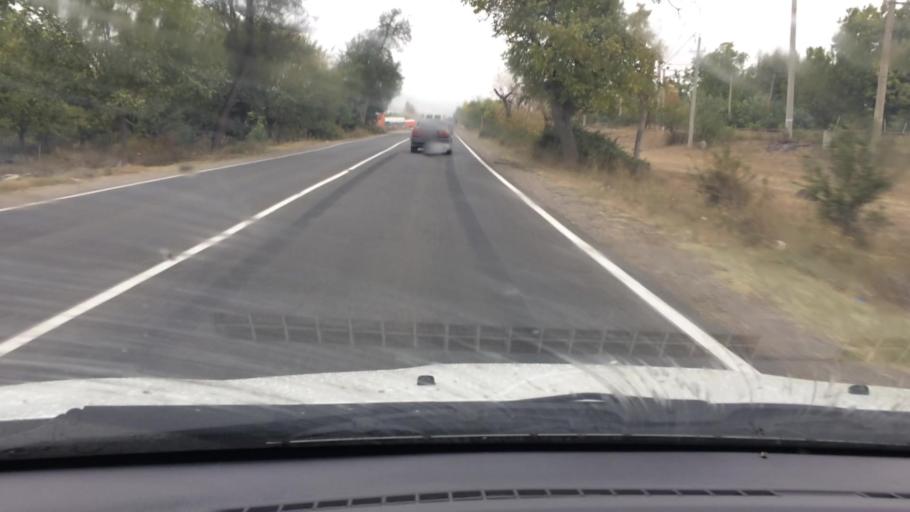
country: GE
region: Kvemo Kartli
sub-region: Marneuli
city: Marneuli
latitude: 41.4164
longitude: 44.8266
